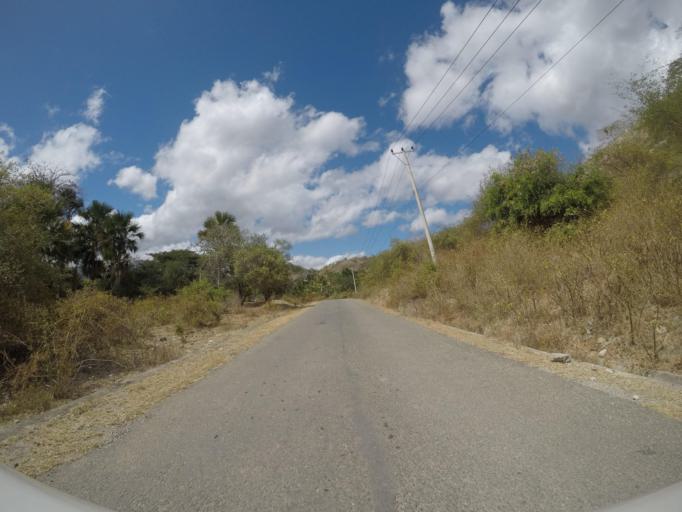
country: TL
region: Lautem
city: Lospalos
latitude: -8.4158
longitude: 126.8264
